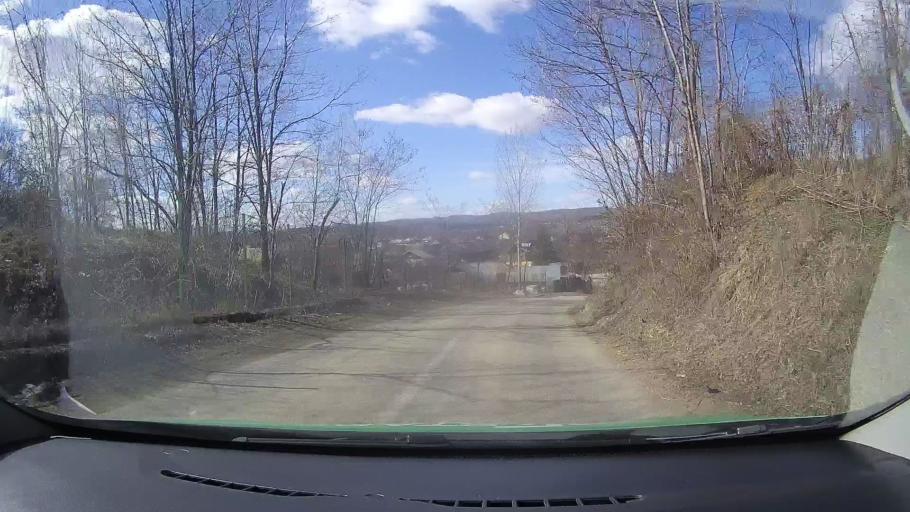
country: RO
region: Dambovita
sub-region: Comuna Glodeni
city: Laculete
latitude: 45.0247
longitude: 25.4250
